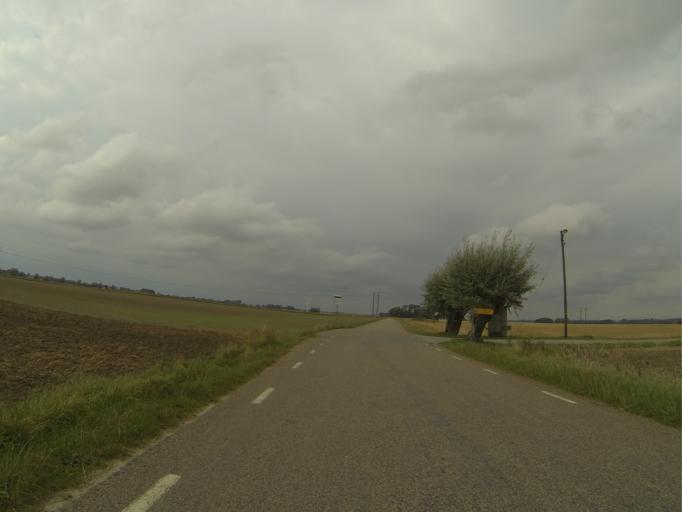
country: SE
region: Skane
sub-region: Lunds Kommun
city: Lund
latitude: 55.7791
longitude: 13.2042
